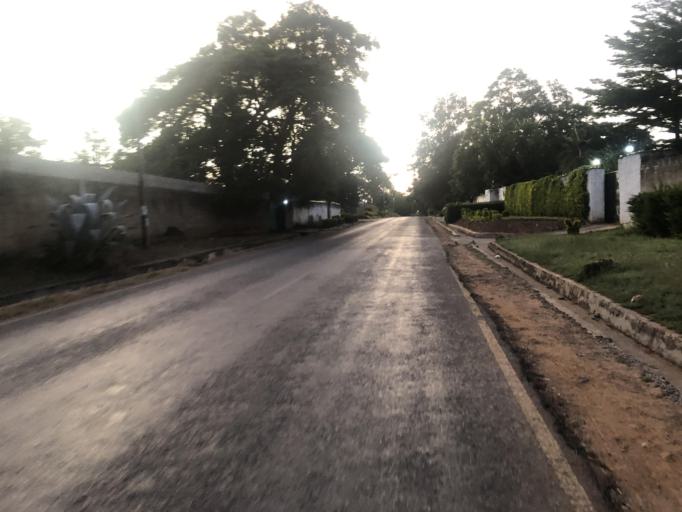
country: ZM
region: Lusaka
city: Lusaka
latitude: -15.3891
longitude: 28.3381
